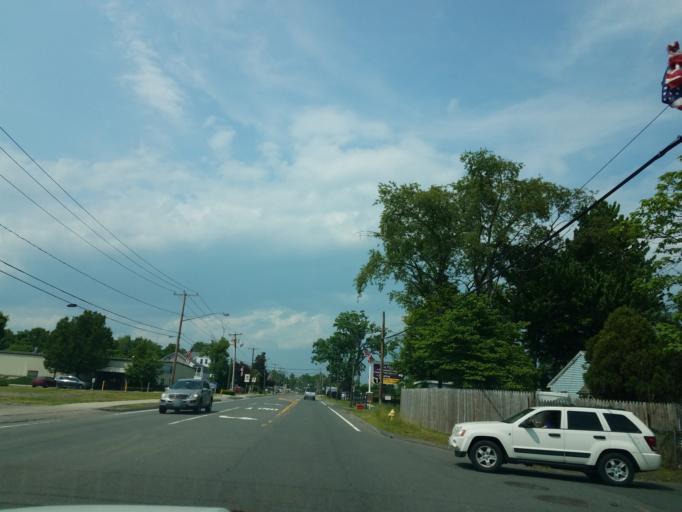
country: US
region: Massachusetts
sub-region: Hampden County
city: Agawam
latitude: 42.0331
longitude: -72.6168
